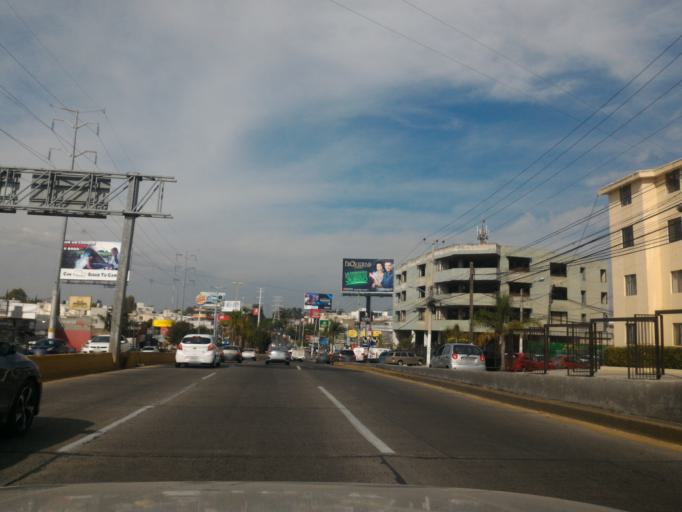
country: MX
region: Jalisco
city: Guadalajara
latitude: 20.6845
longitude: -103.4204
